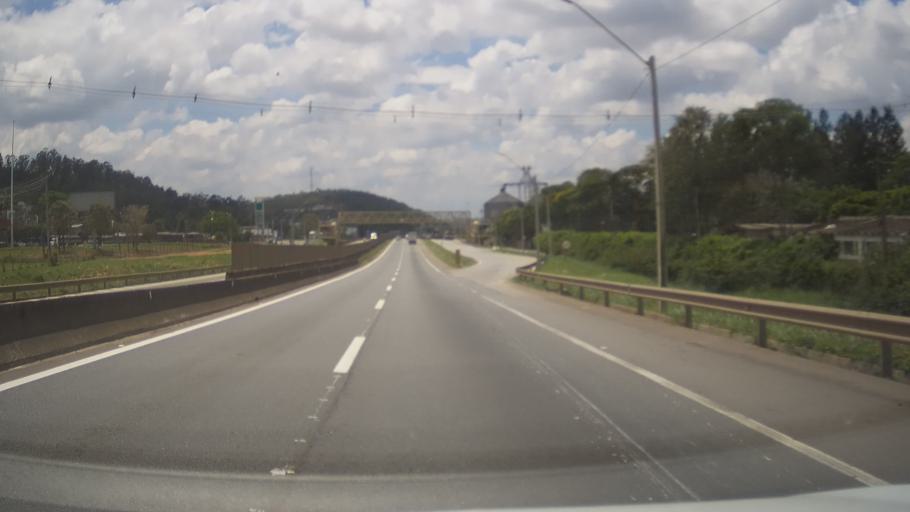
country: BR
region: Minas Gerais
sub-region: Tres Coracoes
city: Tres Coracoes
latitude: -21.6693
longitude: -45.3275
